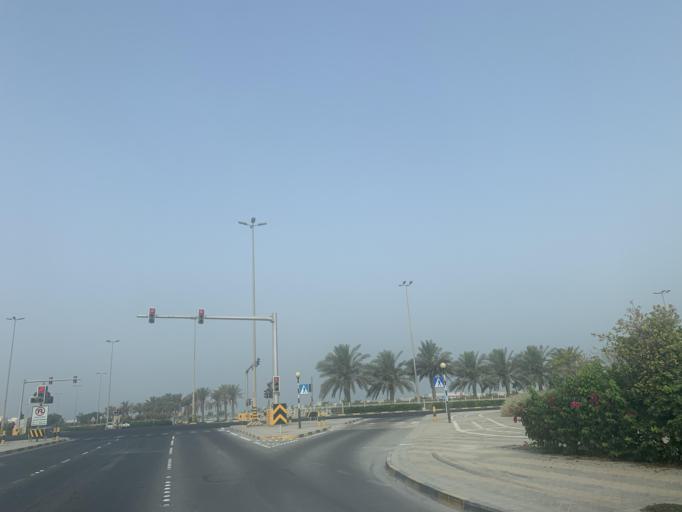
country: BH
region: Manama
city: Jidd Hafs
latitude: 26.2279
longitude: 50.4505
